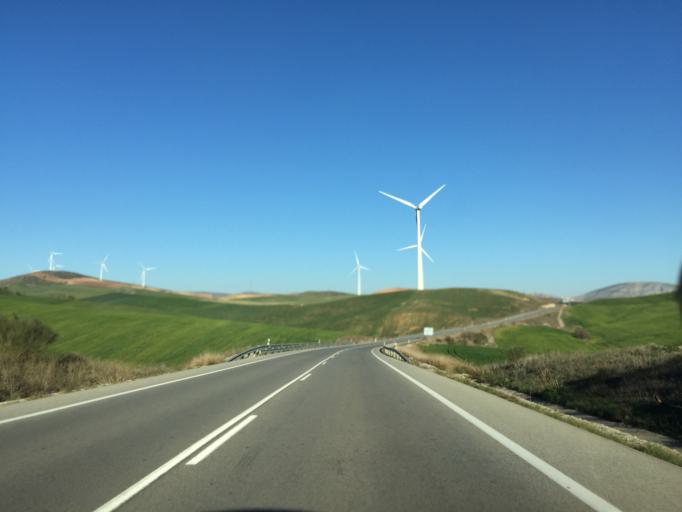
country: ES
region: Andalusia
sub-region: Provincia de Malaga
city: Ardales
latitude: 36.9315
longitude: -4.8581
